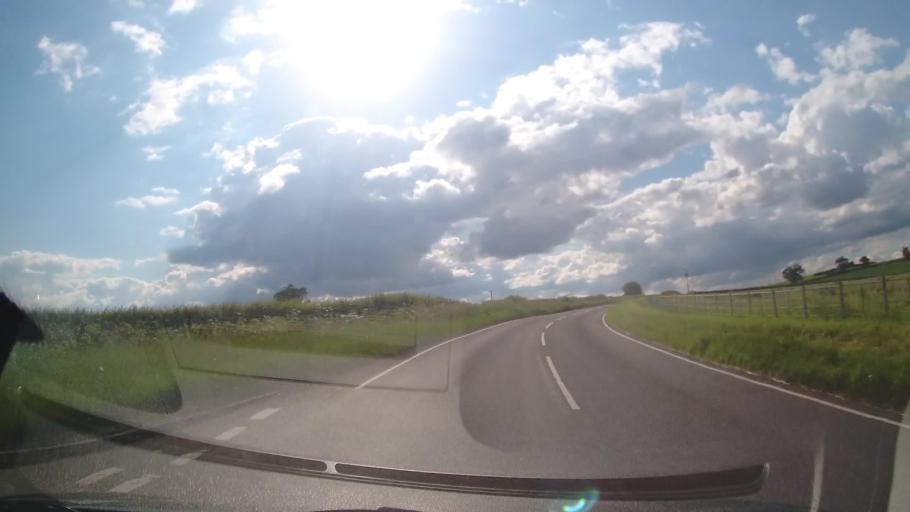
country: GB
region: England
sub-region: Shropshire
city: Harley
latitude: 52.6481
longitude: -2.5991
